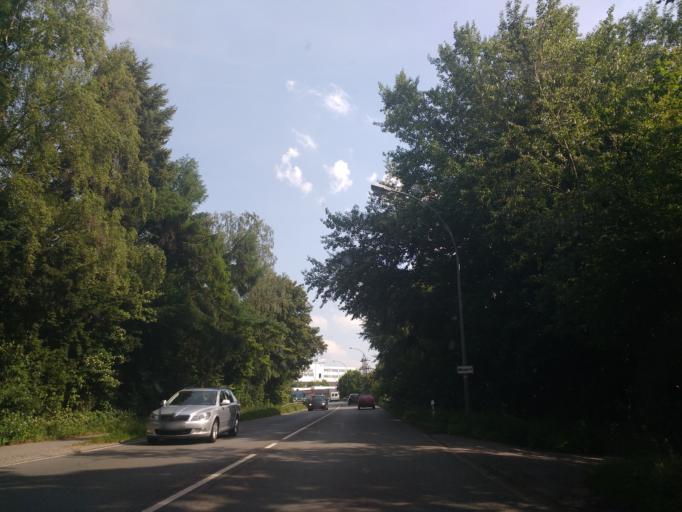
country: DE
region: North Rhine-Westphalia
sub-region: Regierungsbezirk Detmold
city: Bad Salzuflen
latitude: 52.0599
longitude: 8.7508
